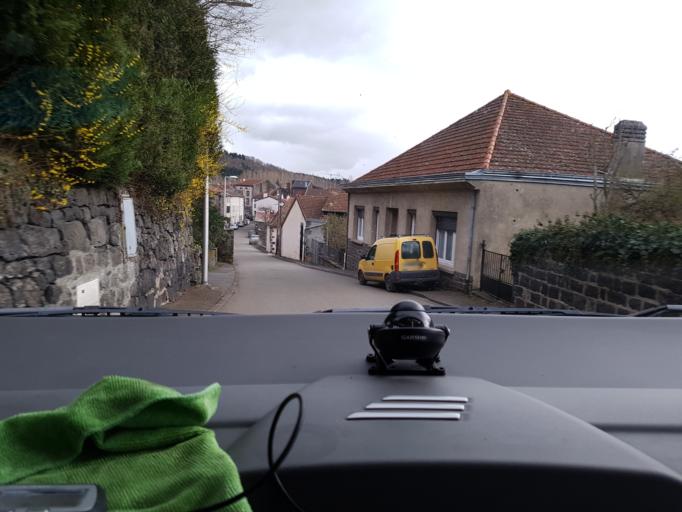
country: FR
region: Auvergne
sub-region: Departement du Puy-de-Dome
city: Saint-Ours
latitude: 45.8348
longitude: 2.8504
